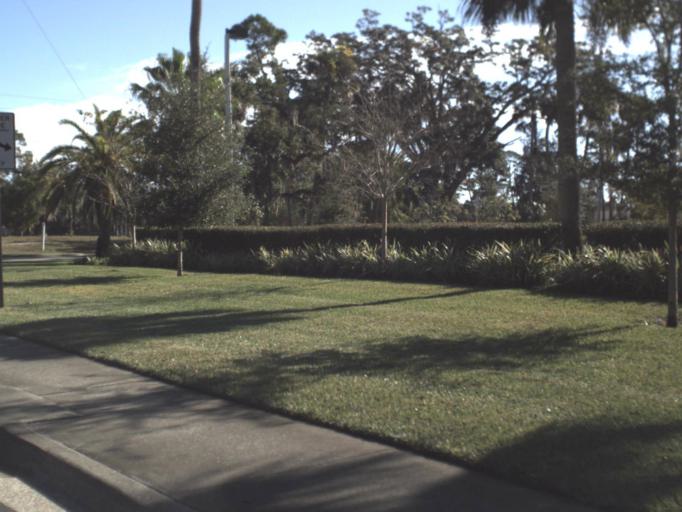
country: US
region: Florida
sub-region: Volusia County
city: Daytona Beach
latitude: 29.2120
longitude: -81.0414
